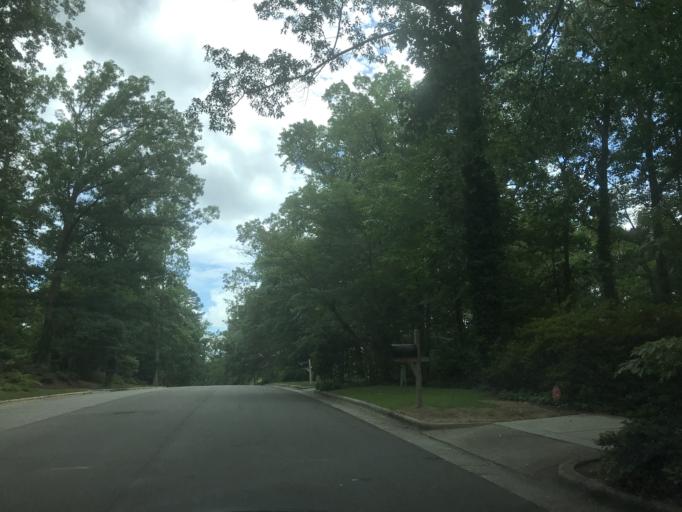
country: US
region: North Carolina
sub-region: Wake County
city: West Raleigh
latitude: 35.8309
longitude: -78.6537
